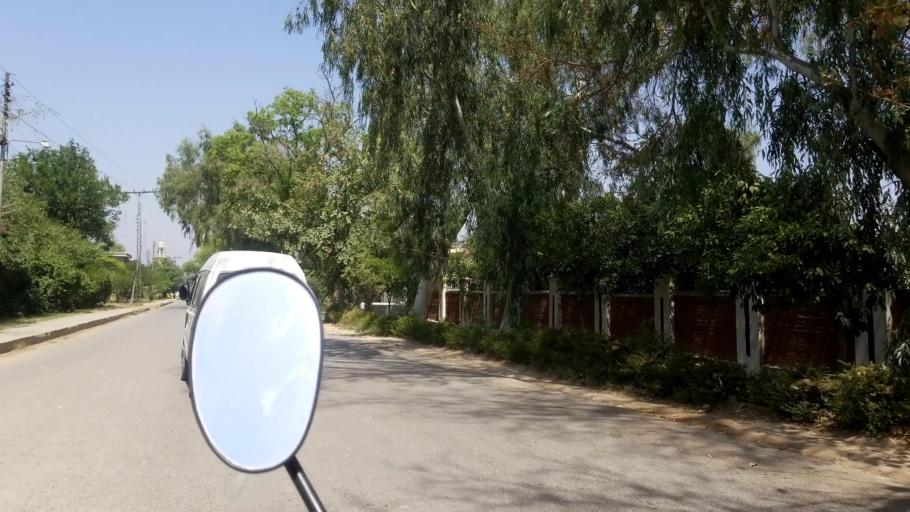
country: PK
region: Khyber Pakhtunkhwa
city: Peshawar
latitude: 34.0106
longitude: 71.4867
